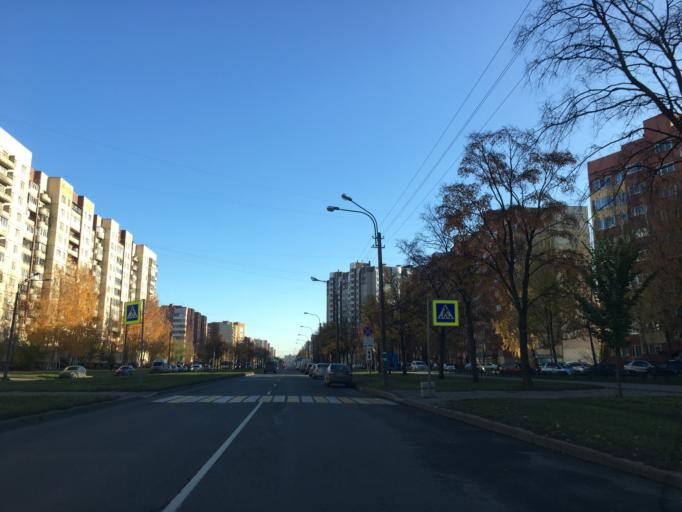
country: RU
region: St.-Petersburg
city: Uritsk
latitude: 59.8563
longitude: 30.1814
